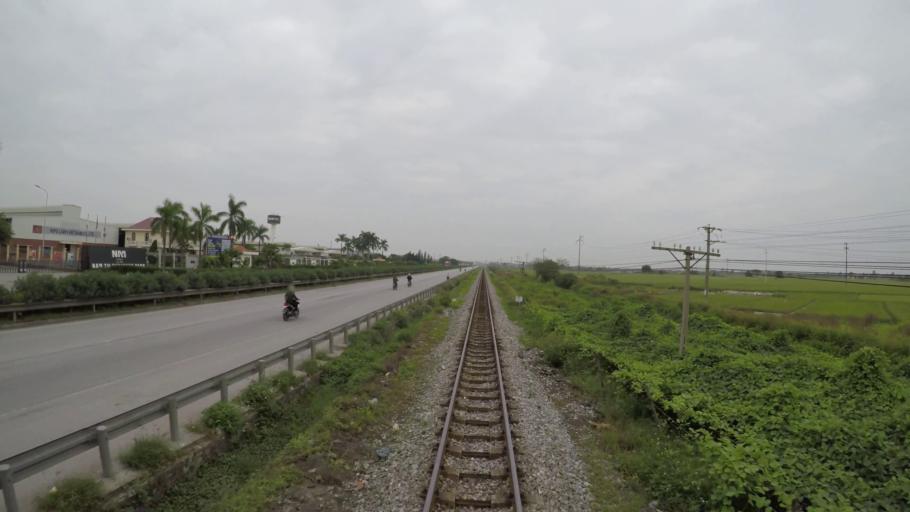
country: VN
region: Hai Duong
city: Phu Thai
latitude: 20.9652
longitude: 106.5141
